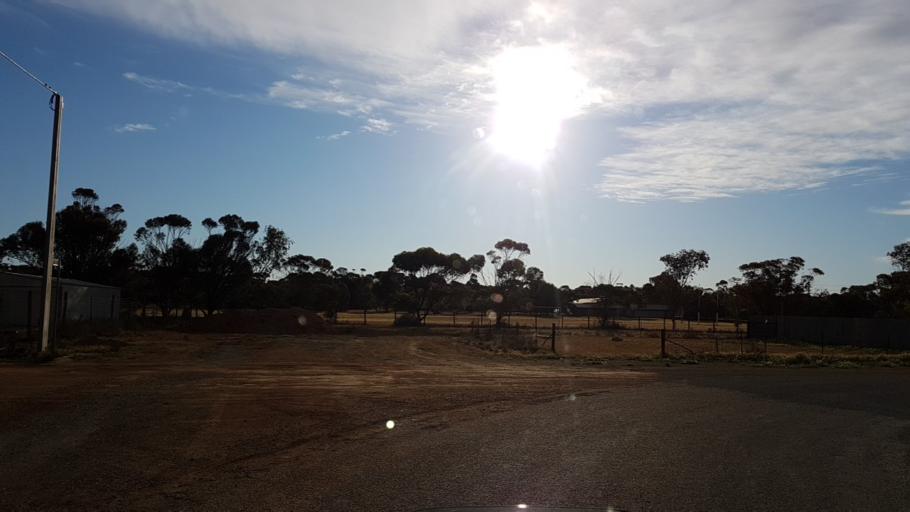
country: AU
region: South Australia
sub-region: Peterborough
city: Peterborough
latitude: -32.9789
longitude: 138.8395
